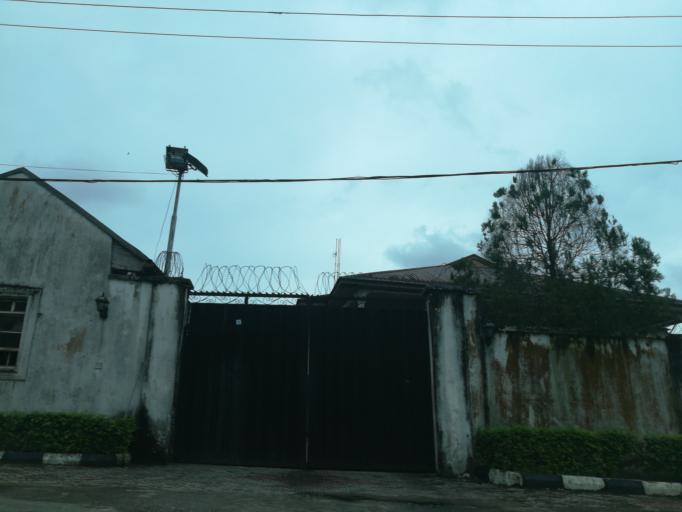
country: NG
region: Rivers
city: Port Harcourt
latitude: 4.8167
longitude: 6.9883
